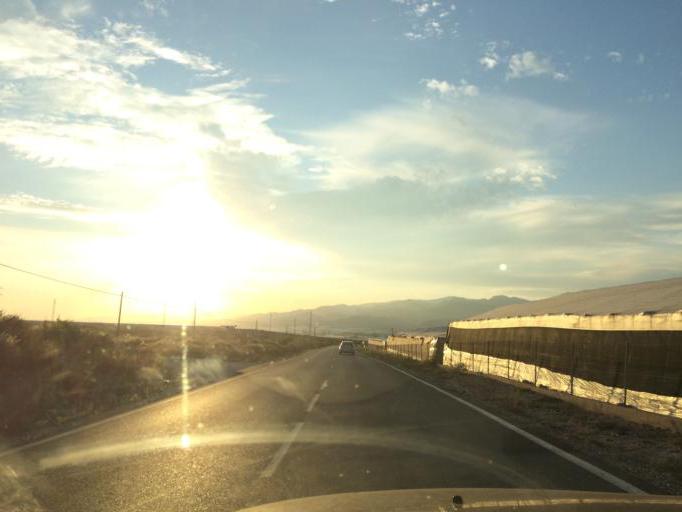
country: ES
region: Andalusia
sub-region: Provincia de Almeria
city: Nijar
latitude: 36.9254
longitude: -2.0854
